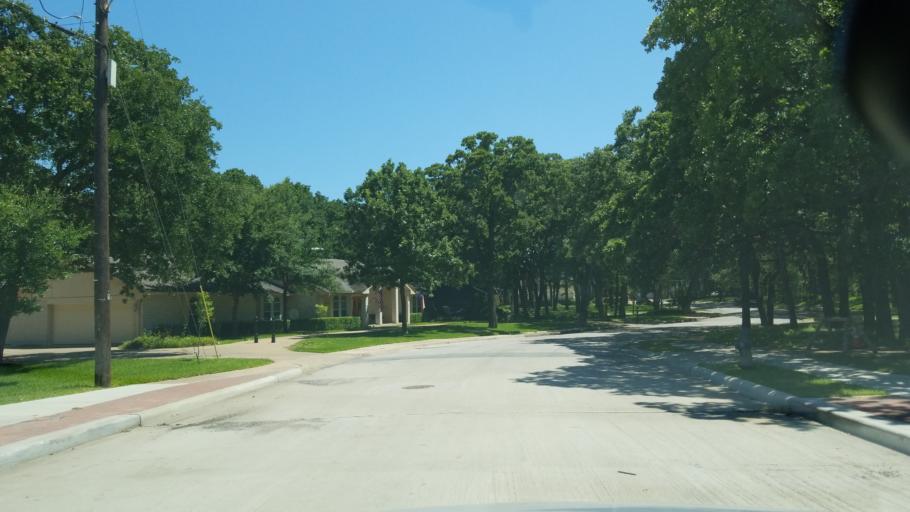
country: US
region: Texas
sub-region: Dallas County
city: Irving
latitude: 32.8308
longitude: -96.9617
